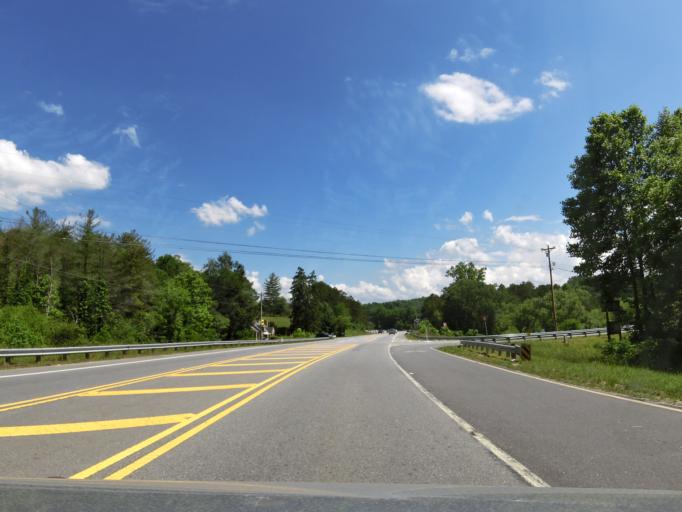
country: US
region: Georgia
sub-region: Union County
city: Blairsville
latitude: 34.8887
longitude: -83.9885
